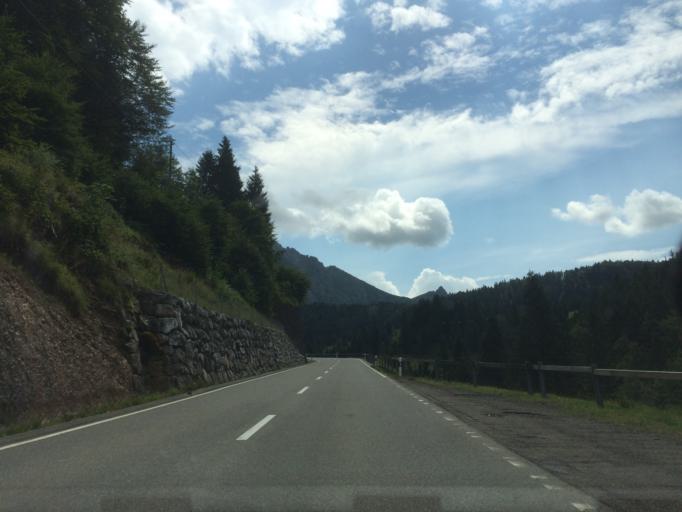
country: CH
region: Appenzell Ausserrhoden
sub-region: Bezirk Hinterland
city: Urnasch
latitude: 47.2696
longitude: 9.2911
